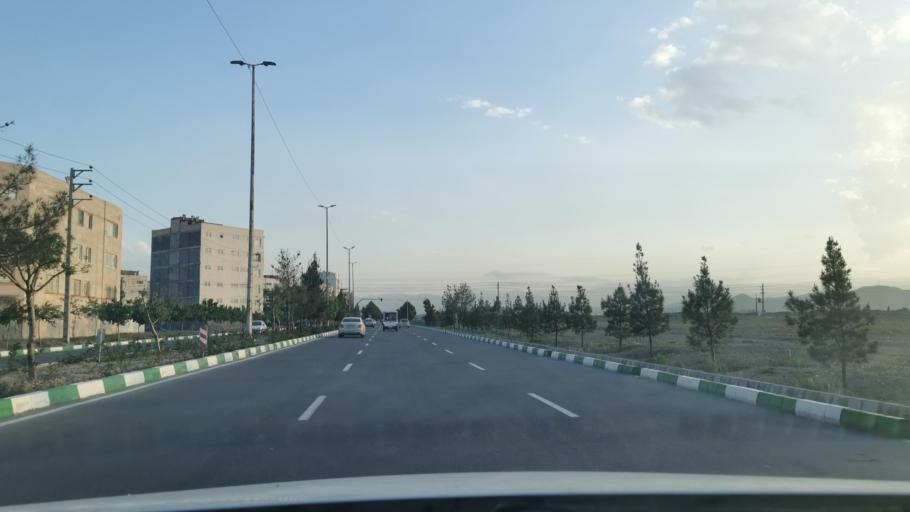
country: IR
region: Razavi Khorasan
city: Mashhad
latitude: 36.3922
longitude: 59.4710
